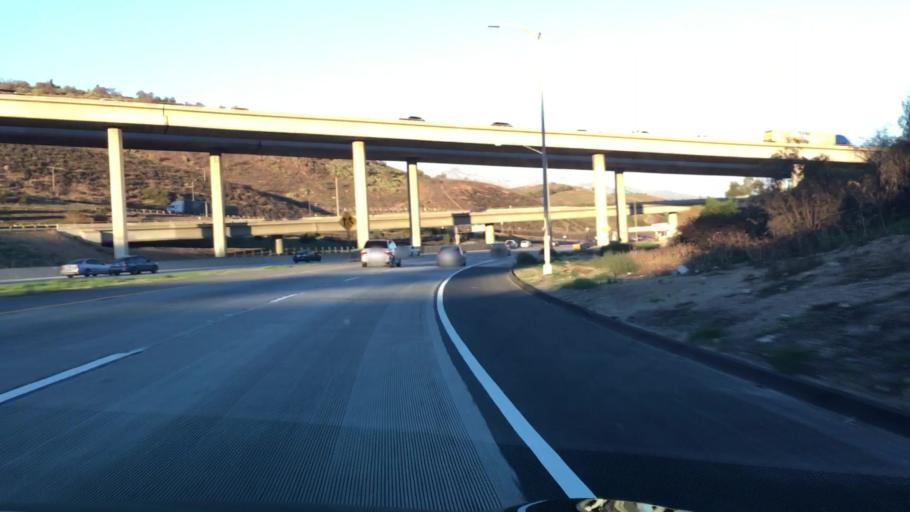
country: US
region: California
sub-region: Los Angeles County
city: Diamond Bar
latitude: 34.0659
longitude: -117.8041
